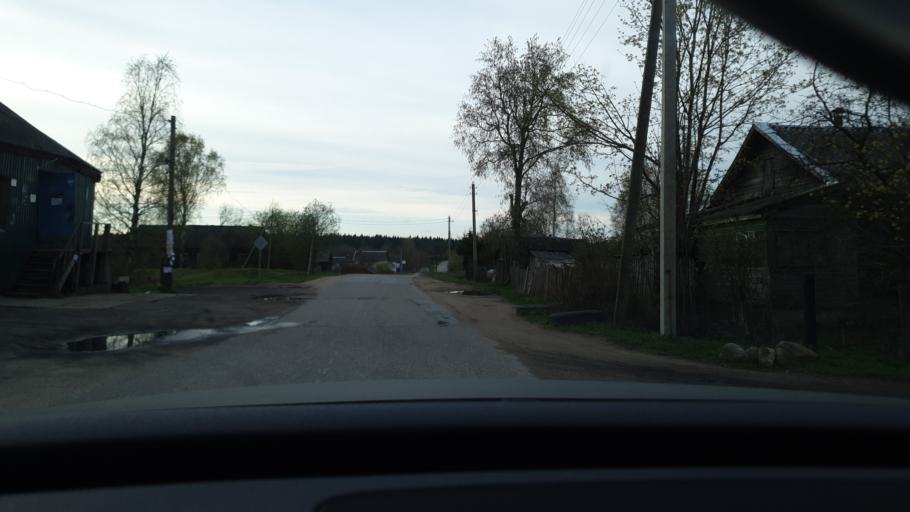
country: RU
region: Tverskaya
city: Berezayka
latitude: 58.0453
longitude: 33.7797
